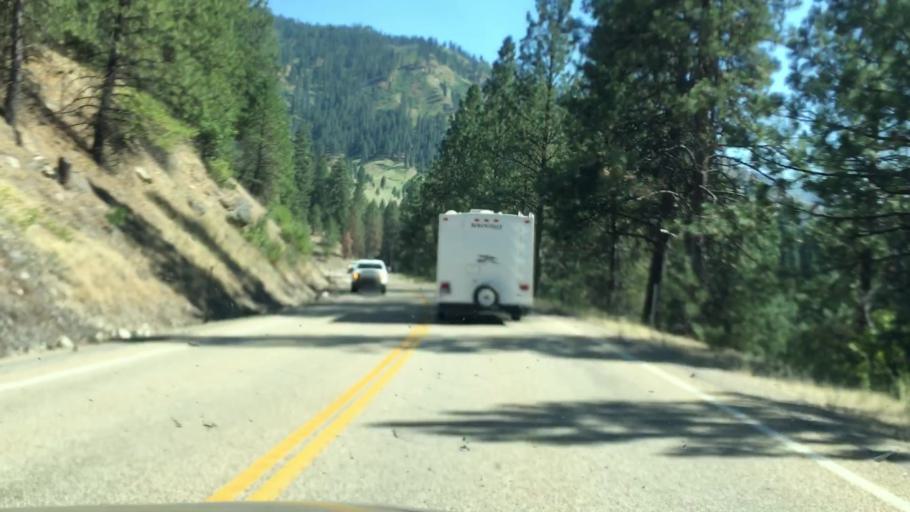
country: US
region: Idaho
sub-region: Boise County
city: Idaho City
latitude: 44.0779
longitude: -116.1215
